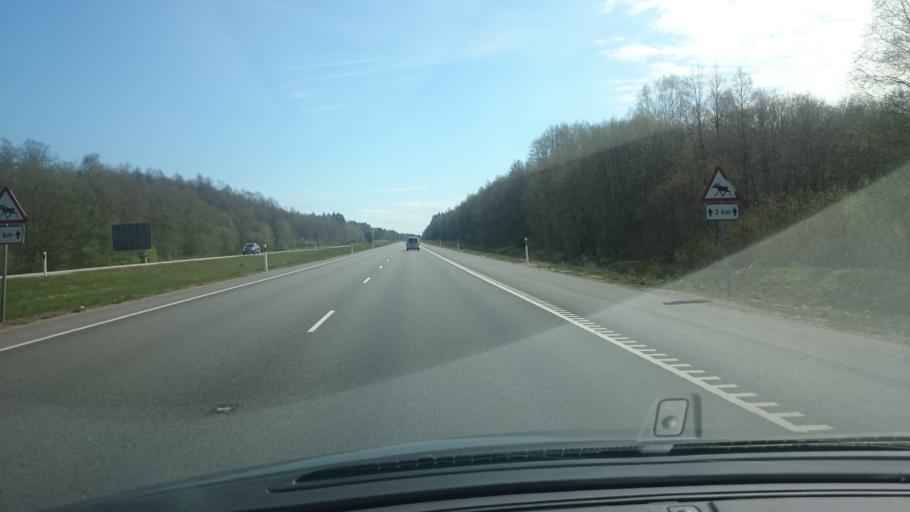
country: EE
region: Harju
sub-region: Loksa linn
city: Loksa
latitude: 59.4637
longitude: 25.7098
